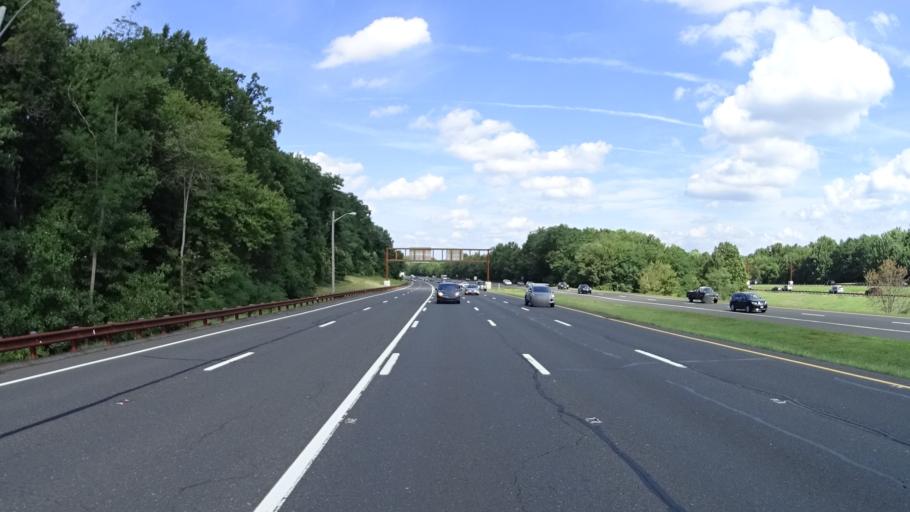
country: US
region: New Jersey
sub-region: Monmouth County
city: Strathmore
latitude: 40.3939
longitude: -74.1834
